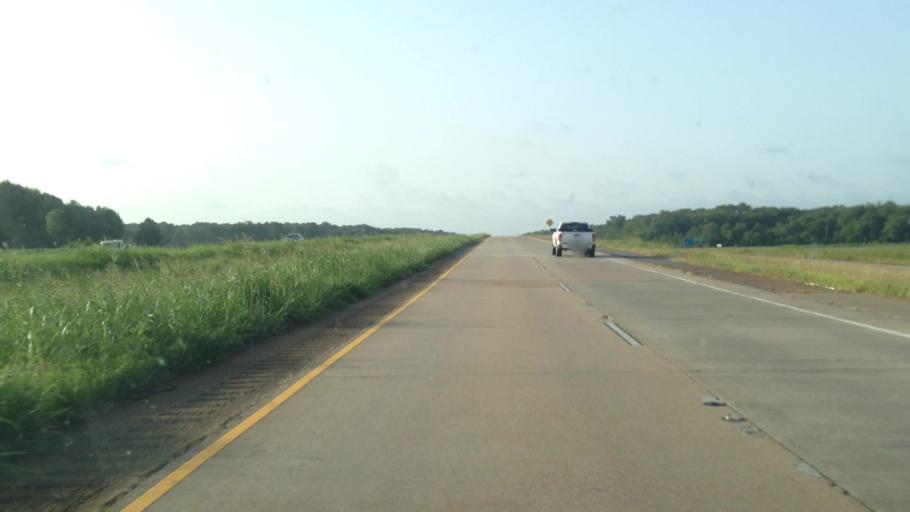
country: US
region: Louisiana
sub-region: Rapides Parish
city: Woodworth
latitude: 31.1683
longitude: -92.4620
